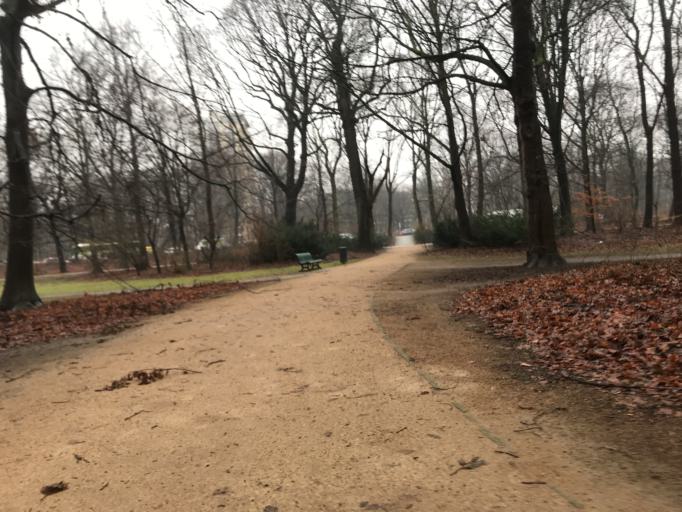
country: DE
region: Berlin
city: Hansaviertel
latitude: 52.5128
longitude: 13.3399
